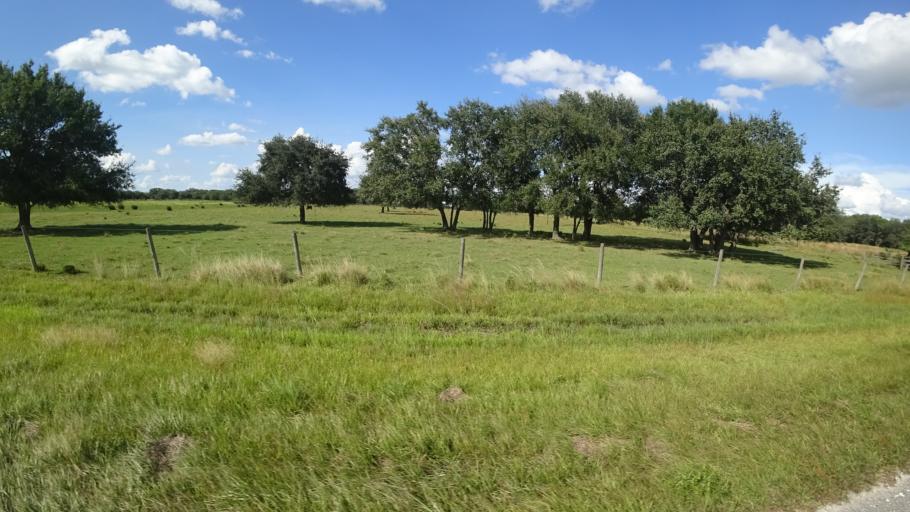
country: US
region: Florida
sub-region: DeSoto County
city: Nocatee
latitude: 27.2709
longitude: -82.0814
